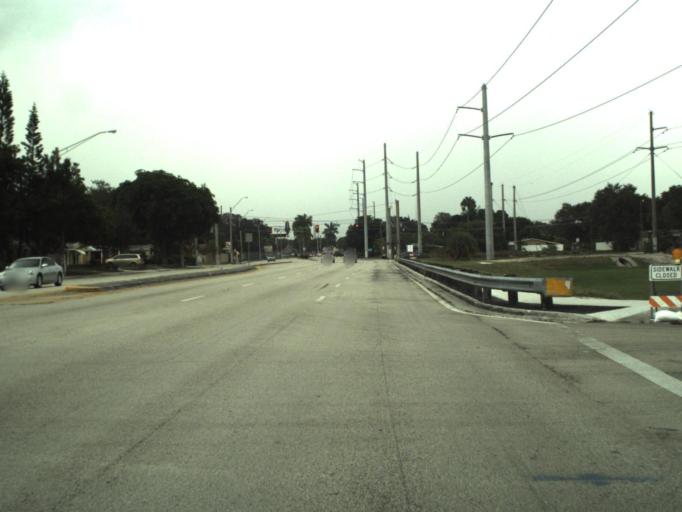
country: US
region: Florida
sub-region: Broward County
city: Pembroke Pines
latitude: 26.0316
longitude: -80.2226
